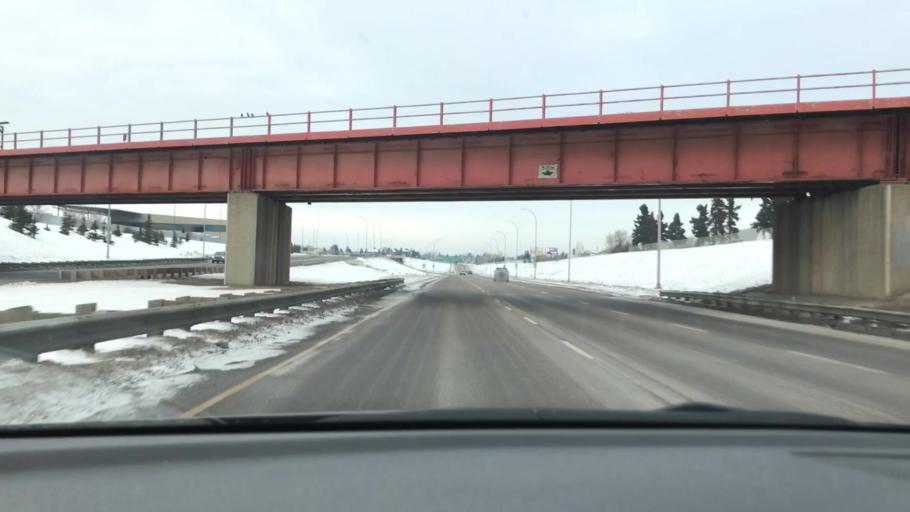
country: CA
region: Alberta
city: Edmonton
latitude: 53.5147
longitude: -113.4241
